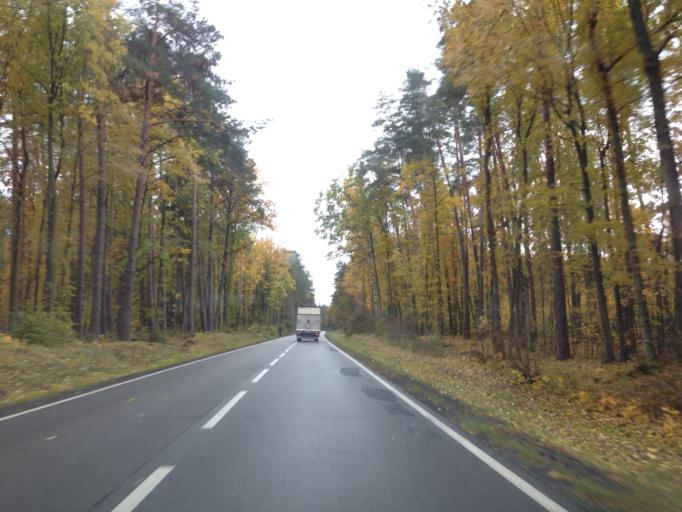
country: PL
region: Pomeranian Voivodeship
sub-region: Powiat kwidzynski
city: Ryjewo
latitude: 53.8425
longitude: 19.0001
